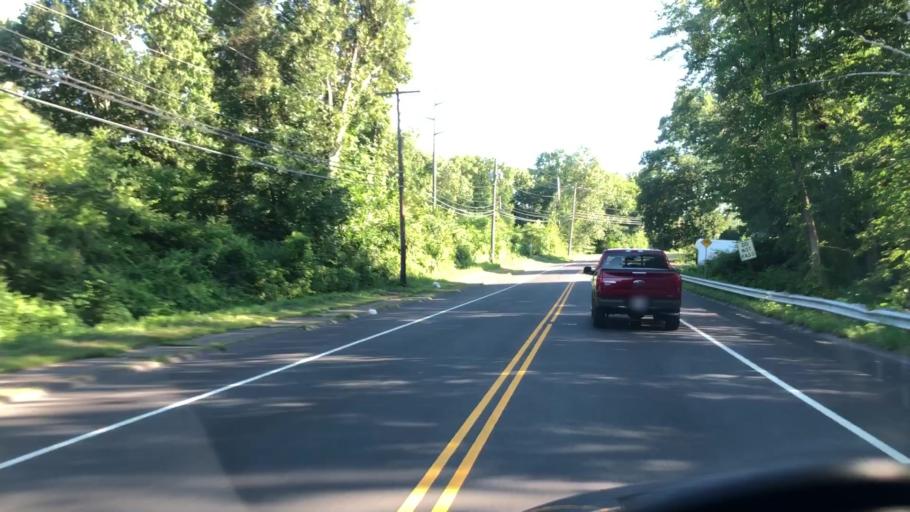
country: US
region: Massachusetts
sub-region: Hampshire County
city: Easthampton
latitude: 42.2792
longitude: -72.6546
